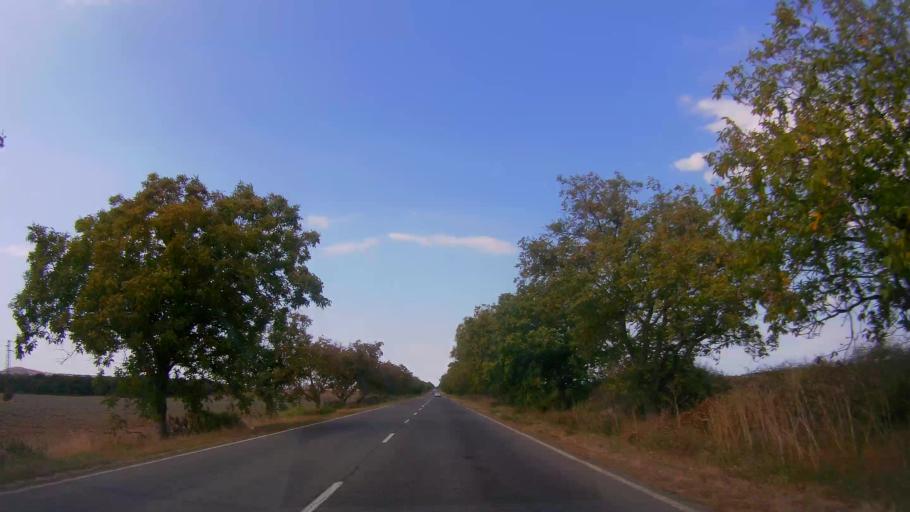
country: BG
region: Burgas
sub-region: Obshtina Aytos
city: Aytos
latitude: 42.6824
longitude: 27.1261
